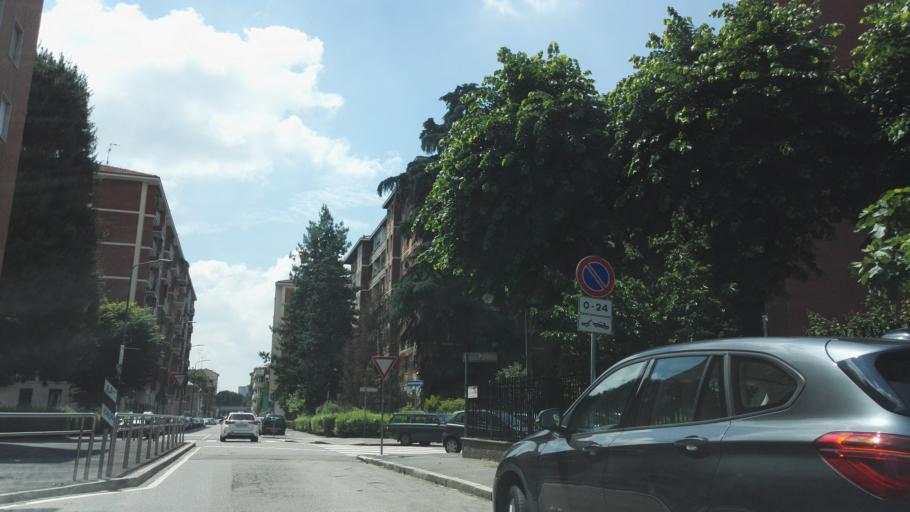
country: IT
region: Lombardy
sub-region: Citta metropolitana di Milano
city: Chiaravalle
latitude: 45.4429
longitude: 9.2278
